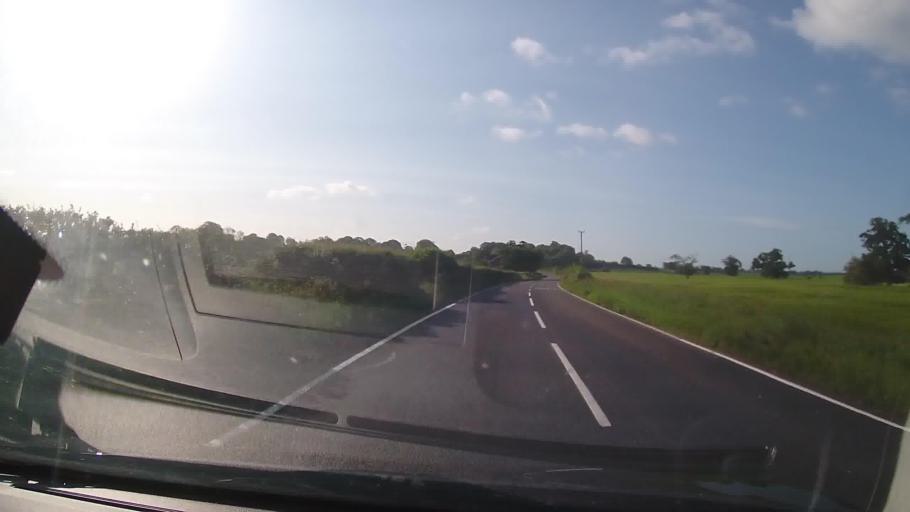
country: GB
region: England
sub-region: Shropshire
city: Wem
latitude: 52.8453
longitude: -2.7162
